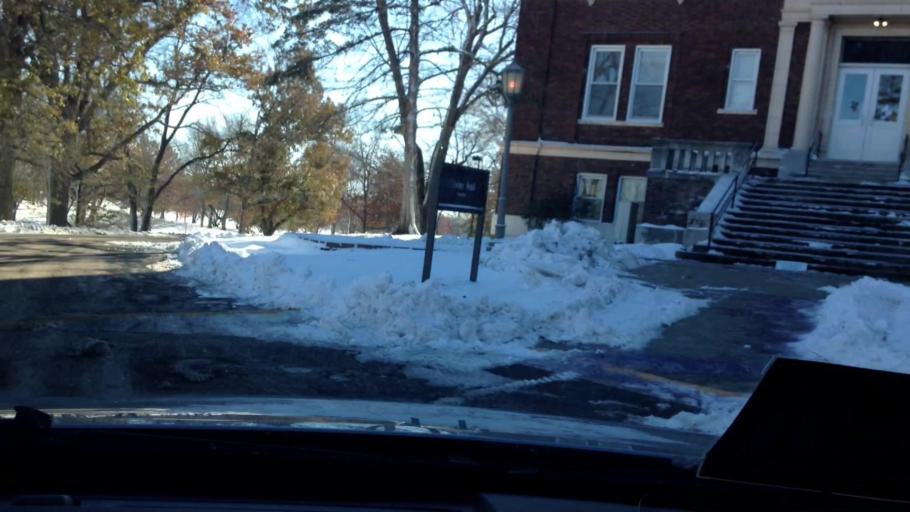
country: US
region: Kansas
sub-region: Leavenworth County
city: Lansing
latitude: 39.2777
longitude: -94.9062
